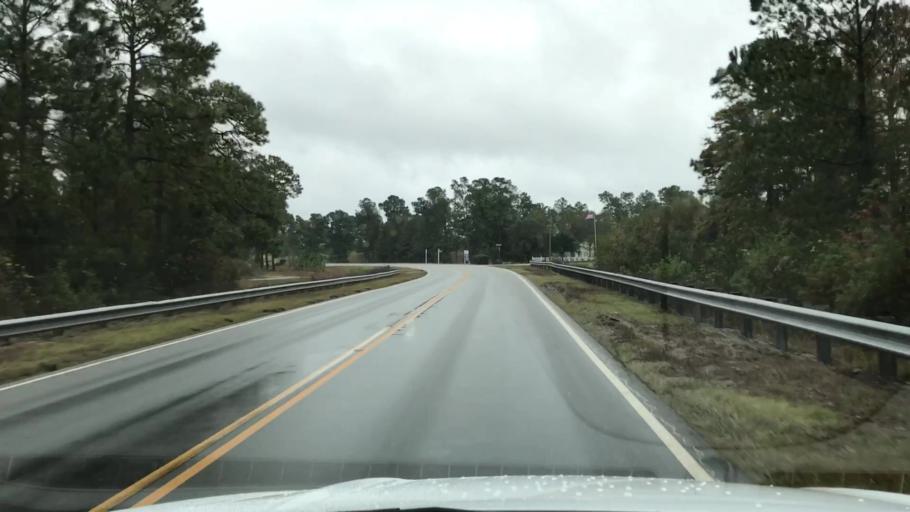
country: US
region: South Carolina
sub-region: Horry County
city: Forestbrook
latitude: 33.7577
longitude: -78.9155
